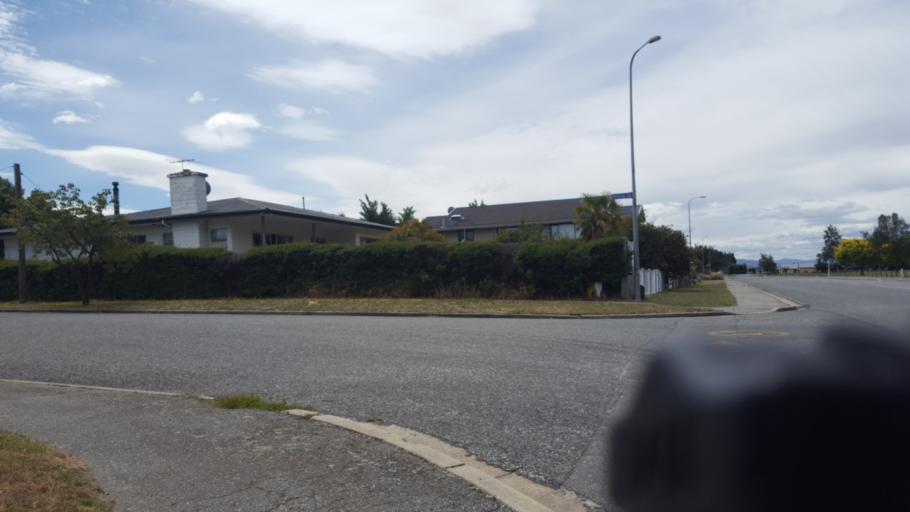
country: NZ
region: Otago
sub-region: Queenstown-Lakes District
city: Wanaka
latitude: -45.0442
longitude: 169.2132
